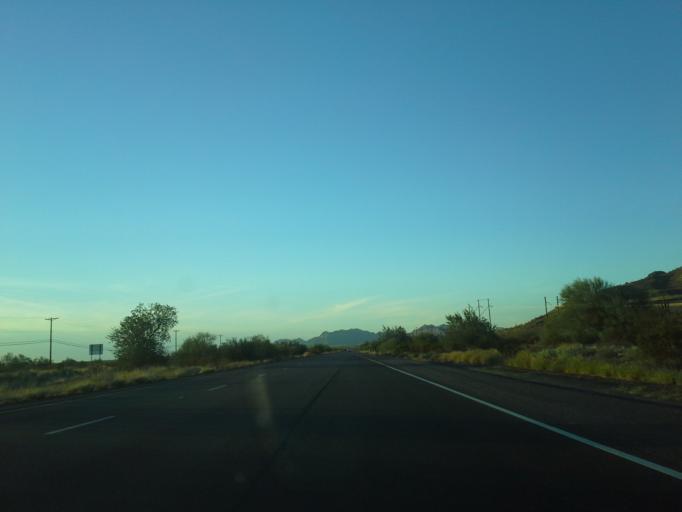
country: US
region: Arizona
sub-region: Pinal County
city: Apache Junction
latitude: 33.3686
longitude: -111.4796
